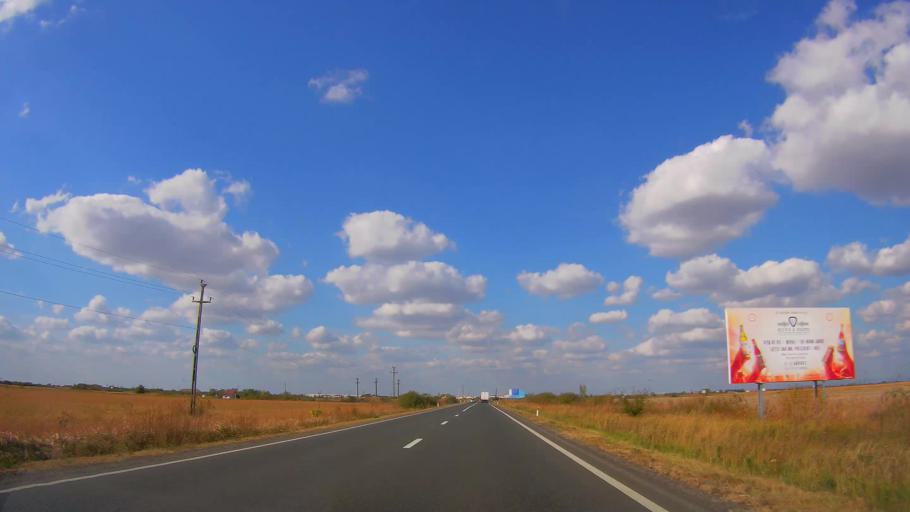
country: RO
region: Satu Mare
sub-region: Oras Ardud
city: Madaras
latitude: 47.7127
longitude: 22.8717
